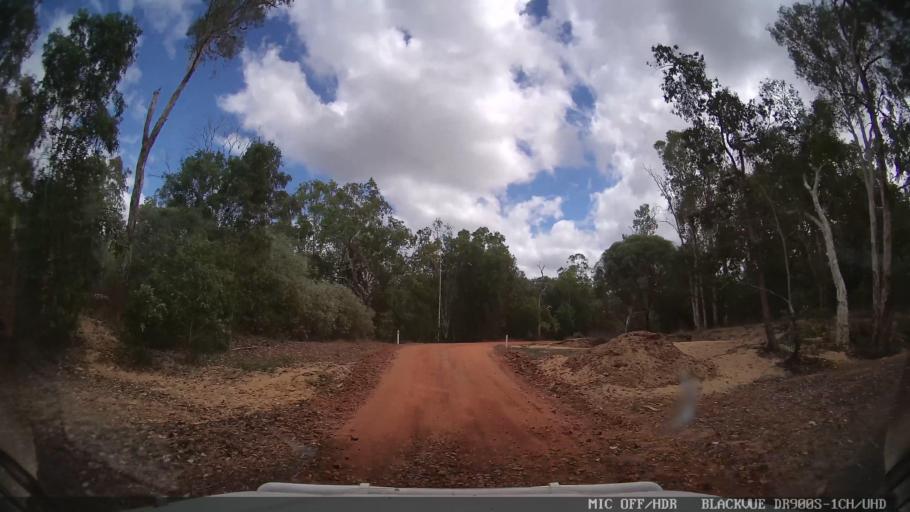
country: AU
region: Queensland
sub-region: Cook
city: Cooktown
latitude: -15.3035
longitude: 144.6168
